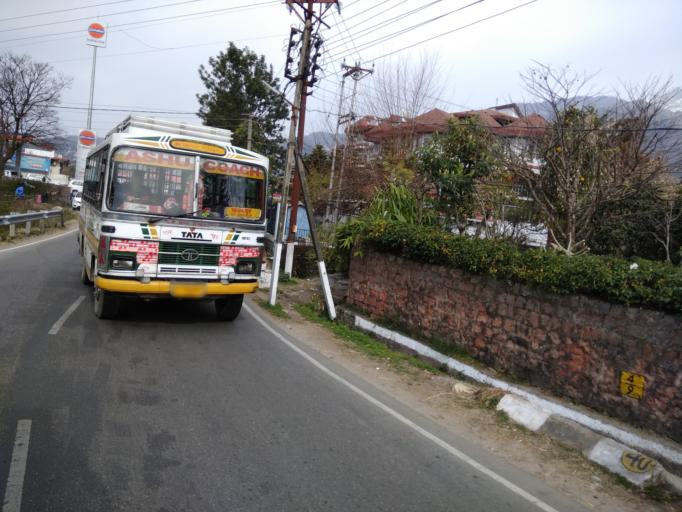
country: IN
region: Himachal Pradesh
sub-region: Kangra
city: Dharmsala
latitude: 32.1942
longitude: 76.3459
